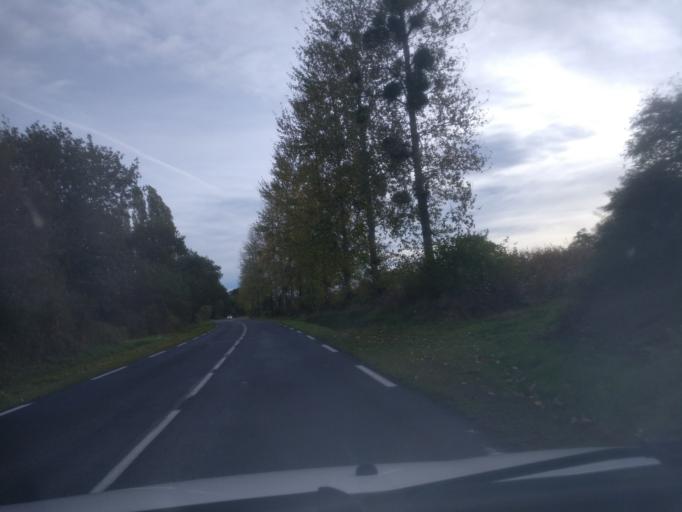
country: FR
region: Lower Normandy
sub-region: Departement de la Manche
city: Jullouville
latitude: 48.7492
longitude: -1.5362
